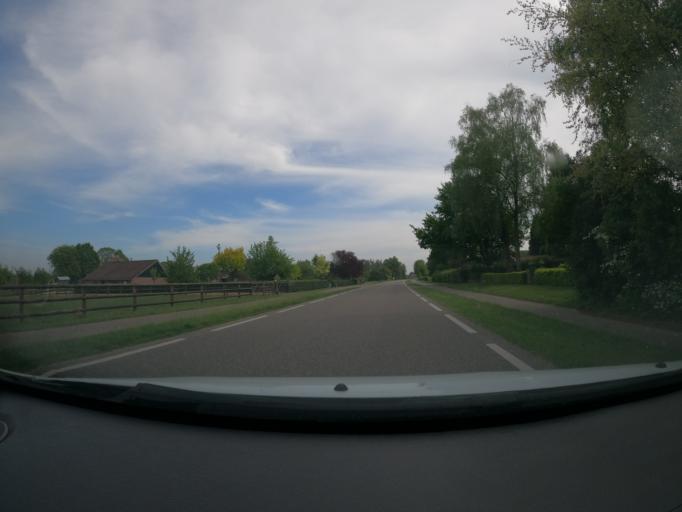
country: NL
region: Gelderland
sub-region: Gemeente Montferland
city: s-Heerenberg
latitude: 51.9198
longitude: 6.2512
